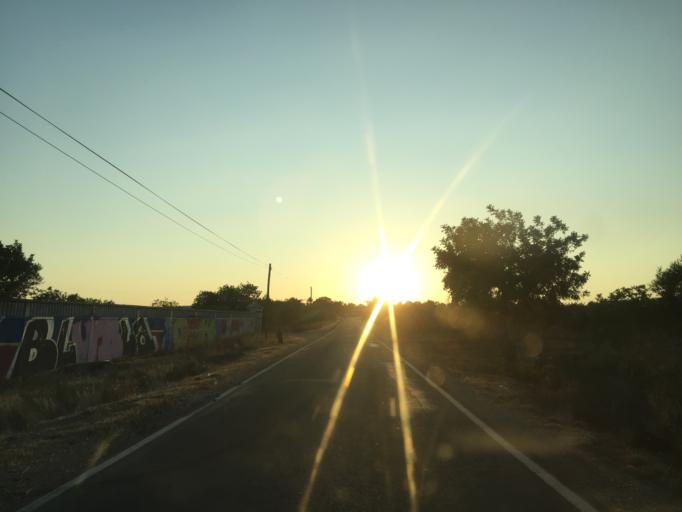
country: PT
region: Faro
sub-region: Faro
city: Santa Barbara de Nexe
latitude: 37.0908
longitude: -7.9335
